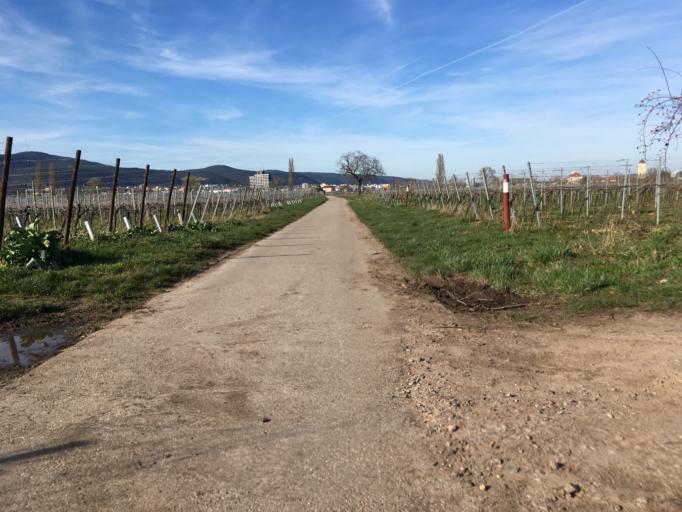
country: DE
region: Rheinland-Pfalz
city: Neustadt
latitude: 49.3319
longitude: 8.1620
